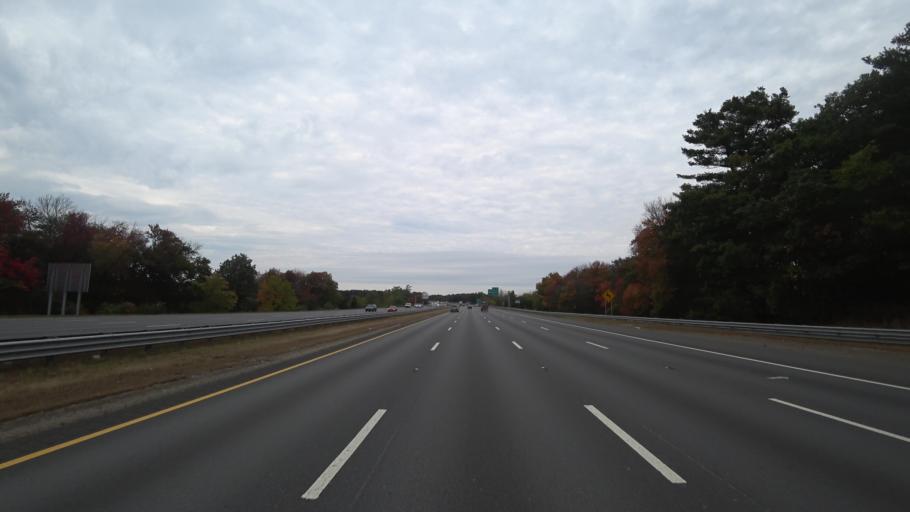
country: US
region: Massachusetts
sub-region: Middlesex County
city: Wilmington
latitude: 42.5483
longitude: -71.1363
